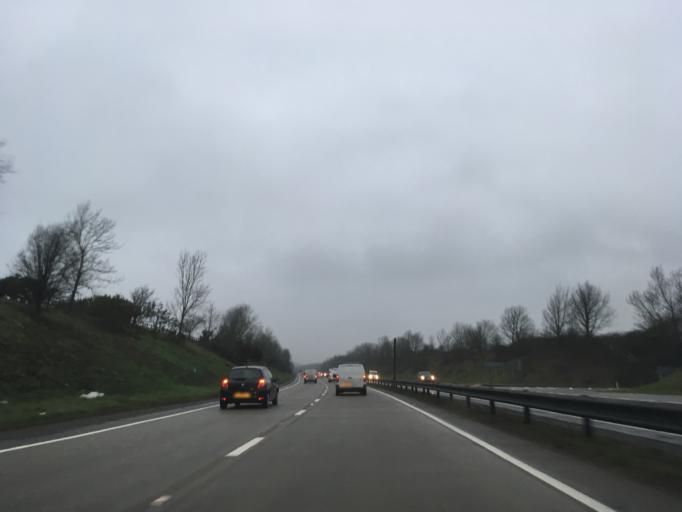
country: GB
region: Wales
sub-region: Cardiff
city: Radyr
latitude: 51.4820
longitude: -3.2828
